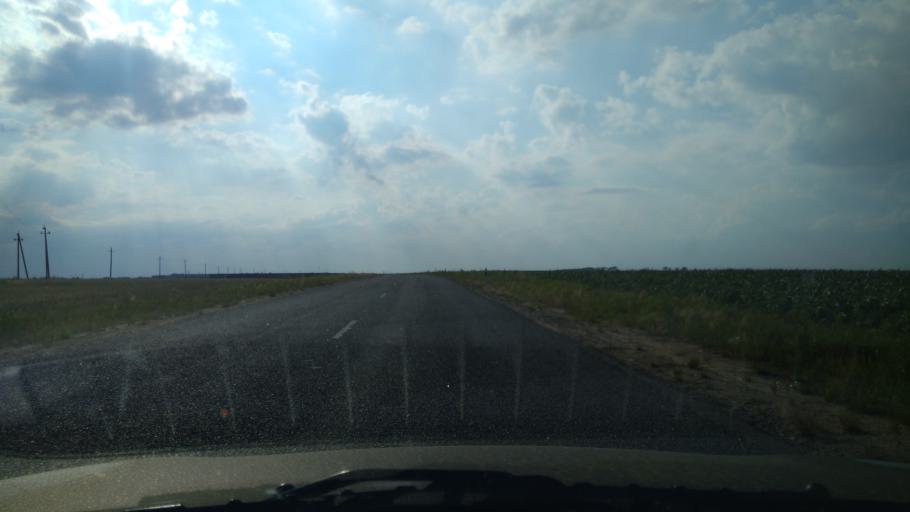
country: BY
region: Brest
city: Lyakhavichy
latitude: 53.0320
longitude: 26.3071
